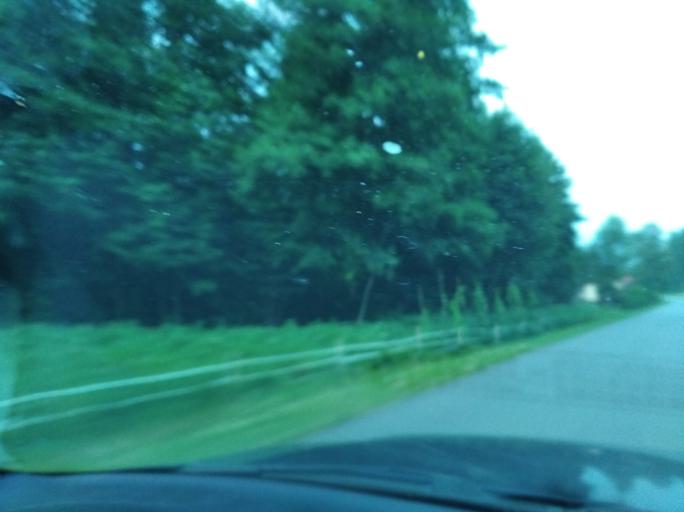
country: PL
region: Subcarpathian Voivodeship
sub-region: Powiat ropczycko-sedziszowski
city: Iwierzyce
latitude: 49.9919
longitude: 21.7265
